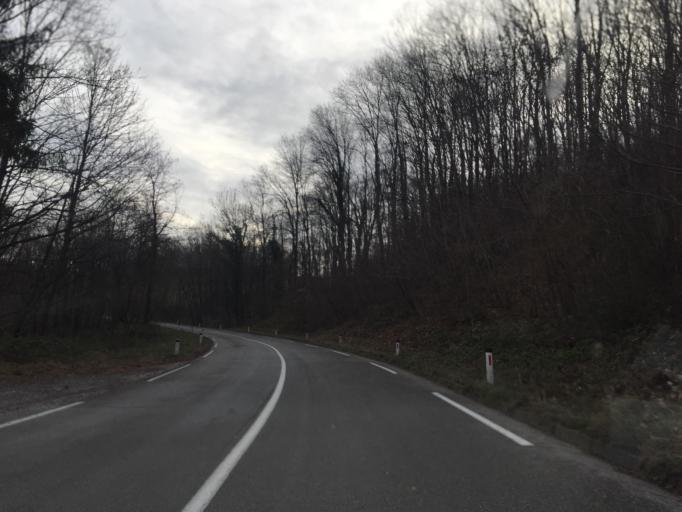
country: SI
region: Nova Gorica
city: Kromberk
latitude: 45.9813
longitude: 13.6826
